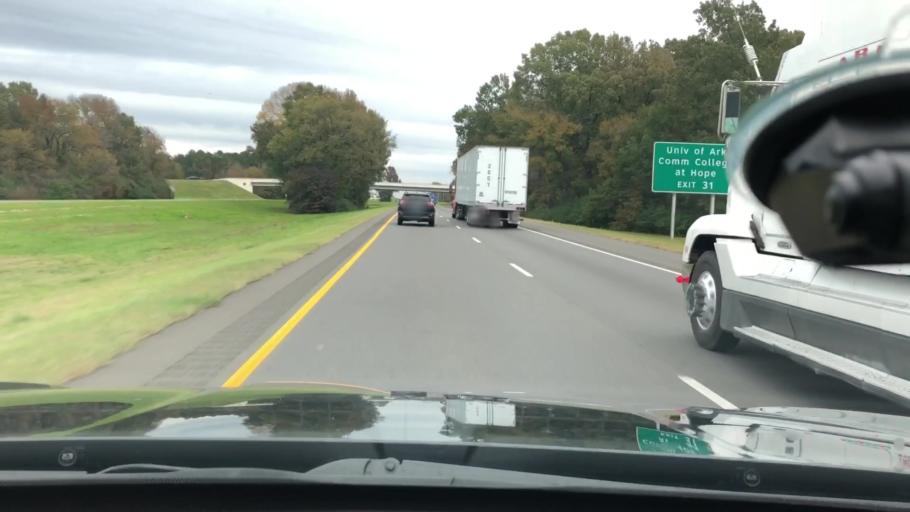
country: US
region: Arkansas
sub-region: Hempstead County
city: Hope
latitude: 33.6801
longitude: -93.6130
